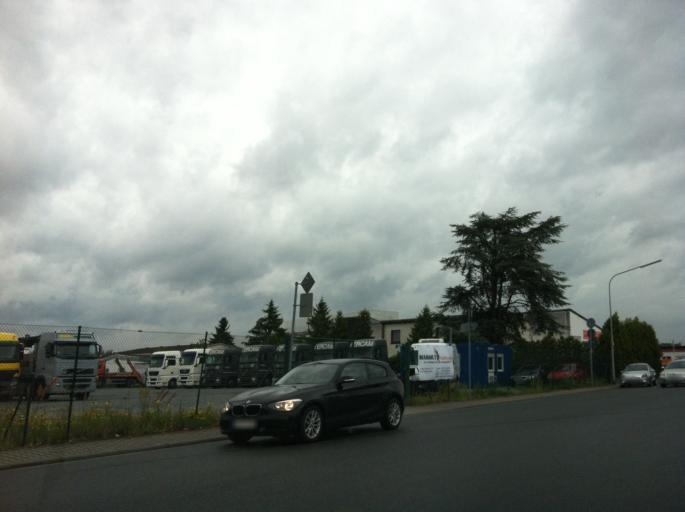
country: DE
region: Hesse
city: Weiterstadt
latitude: 49.8985
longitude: 8.6154
